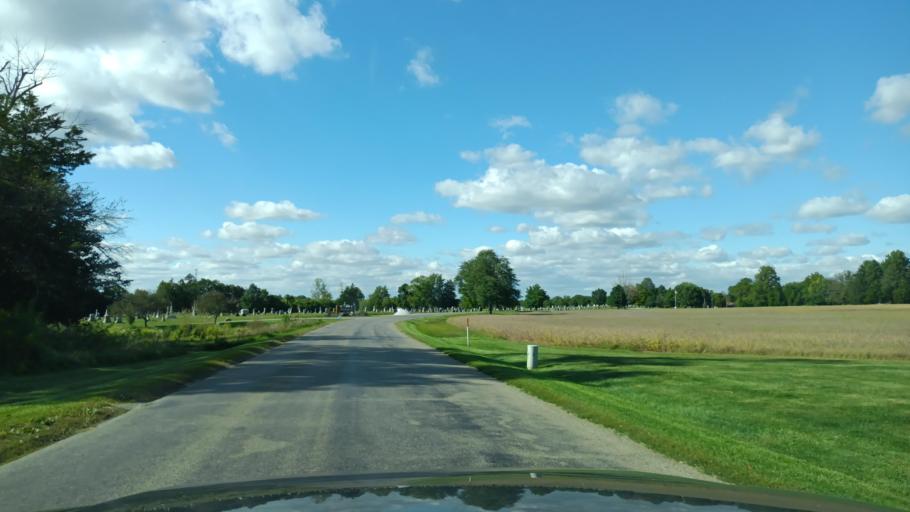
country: US
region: Indiana
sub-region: Fountain County
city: Covington
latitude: 40.1274
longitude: -87.3847
